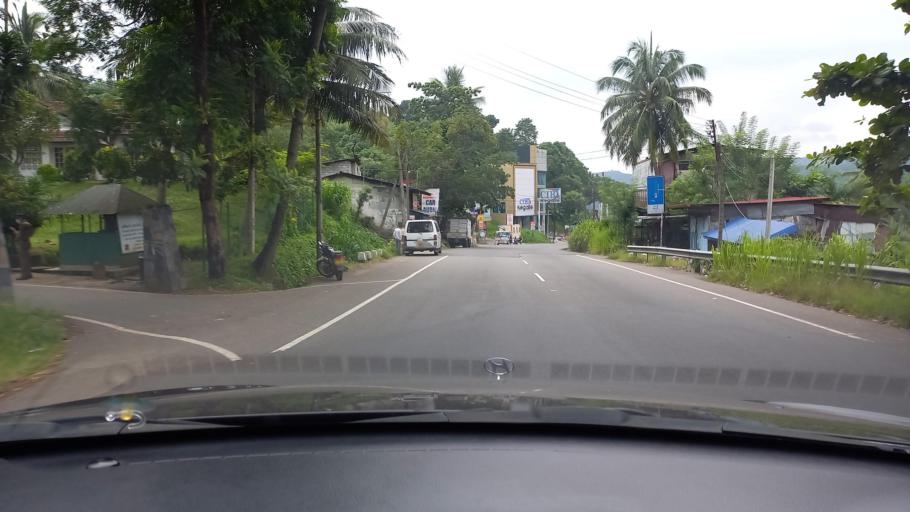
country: LK
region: Central
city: Kadugannawa
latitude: 7.2549
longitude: 80.3539
